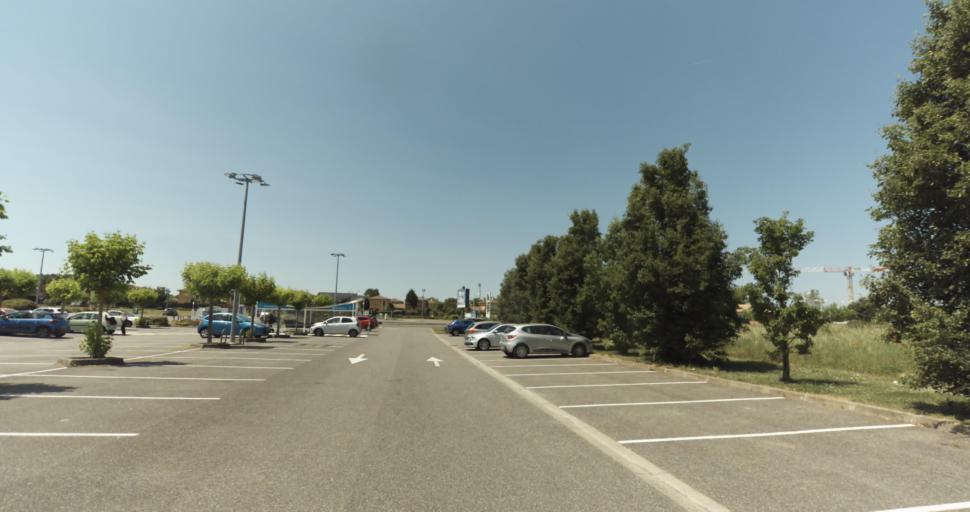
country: FR
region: Midi-Pyrenees
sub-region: Departement de la Haute-Garonne
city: La Salvetat-Saint-Gilles
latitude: 43.6016
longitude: 1.2636
